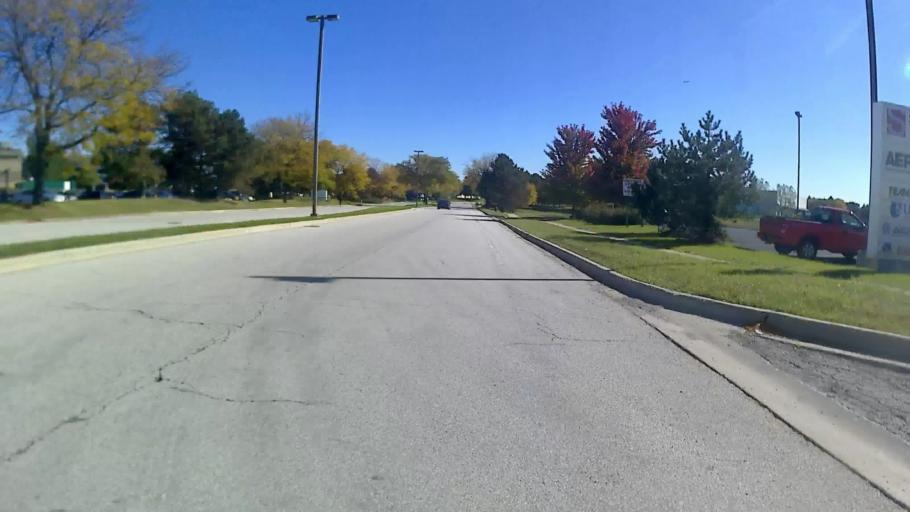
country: US
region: Illinois
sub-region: DuPage County
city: Itasca
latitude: 41.9894
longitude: -87.9888
